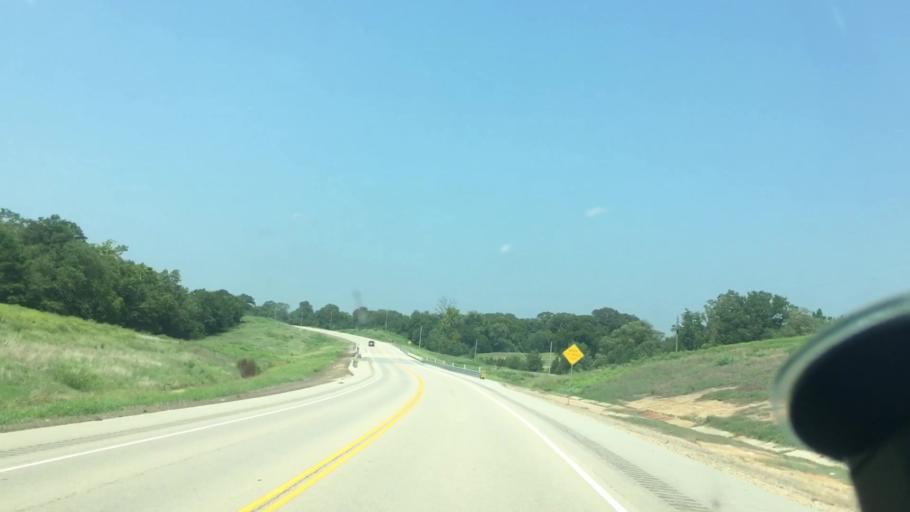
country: US
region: Oklahoma
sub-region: Atoka County
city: Atoka
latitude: 34.2851
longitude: -95.9567
